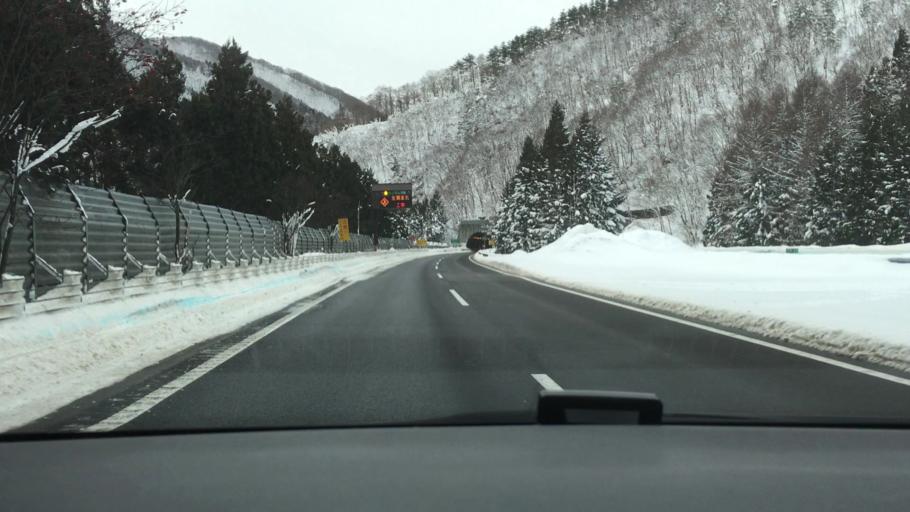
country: JP
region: Akita
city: Hanawa
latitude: 40.1165
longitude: 140.8925
